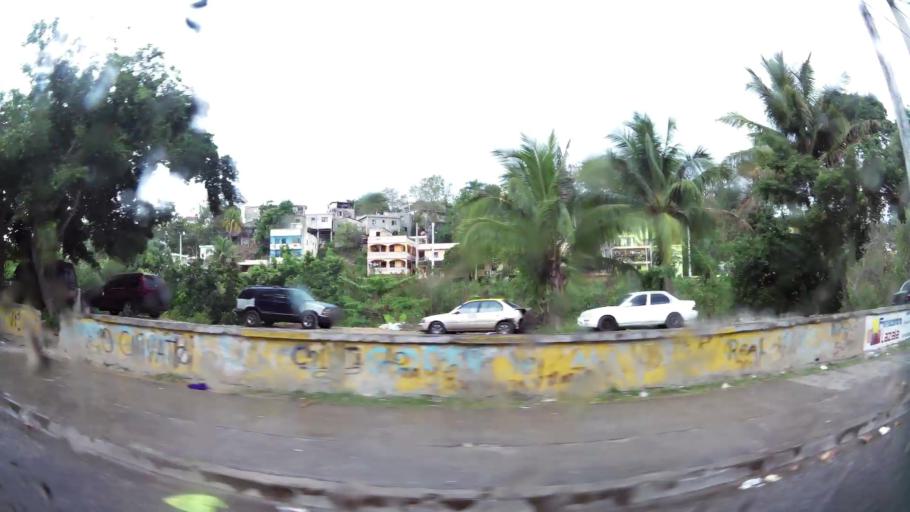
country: DO
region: Nacional
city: La Agustina
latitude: 18.5011
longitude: -69.9318
